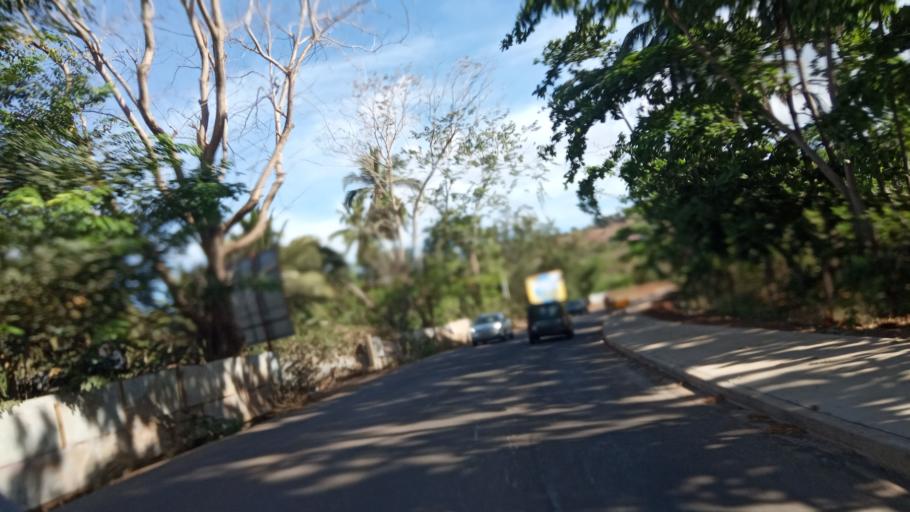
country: YT
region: Dembeni
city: Dembeni
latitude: -12.8404
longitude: 45.1845
